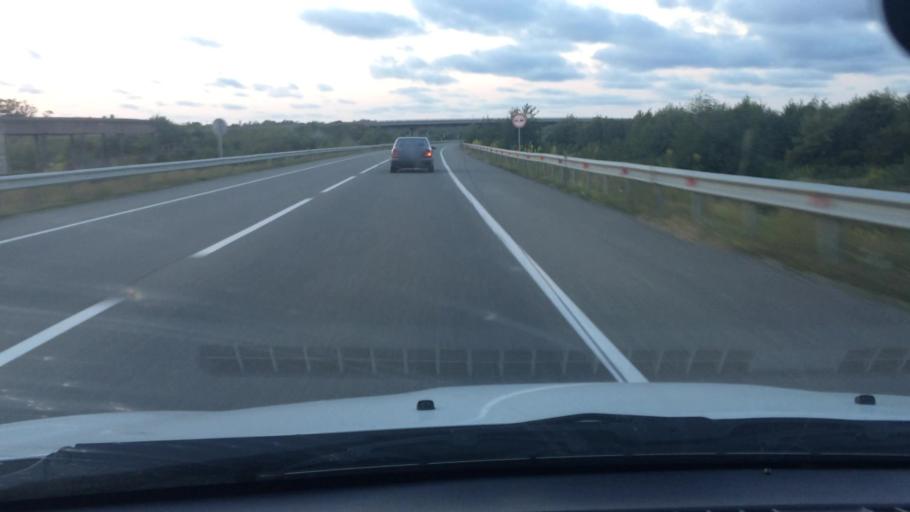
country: GE
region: Guria
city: Urek'i
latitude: 41.9155
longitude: 41.7777
